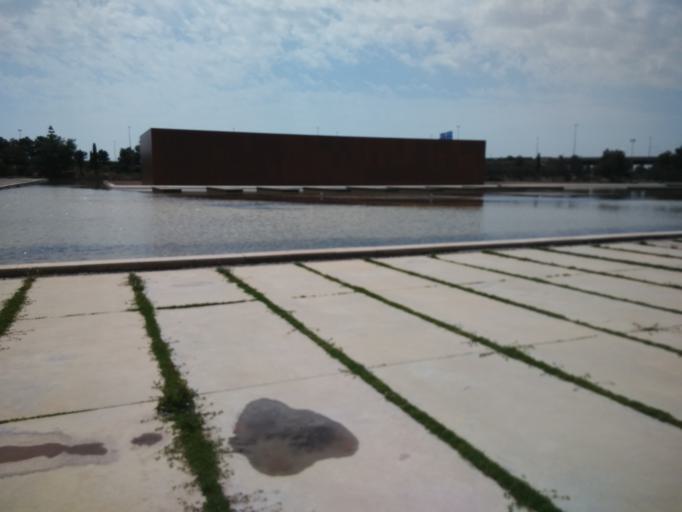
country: ES
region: Valencia
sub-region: Provincia de Alicante
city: San Vicent del Raspeig
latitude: 38.3819
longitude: -0.5117
